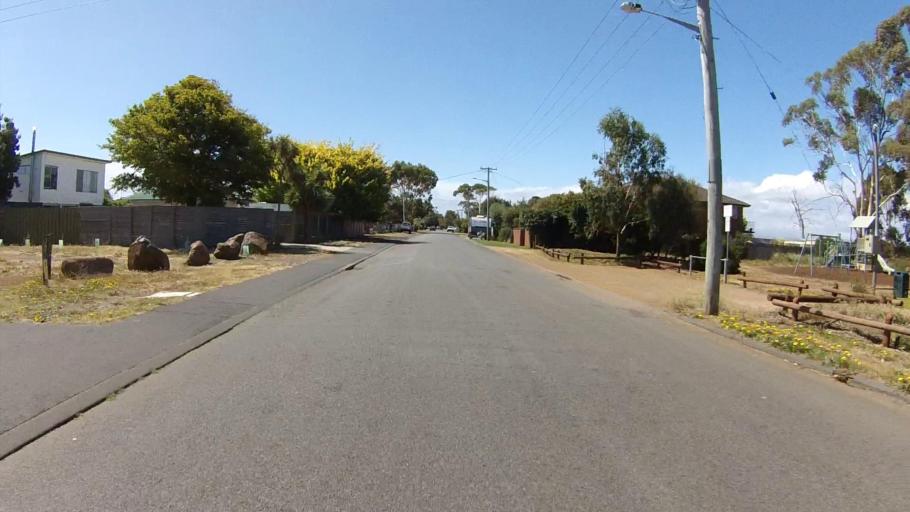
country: AU
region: Tasmania
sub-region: Clarence
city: Lauderdale
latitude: -42.9013
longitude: 147.4955
